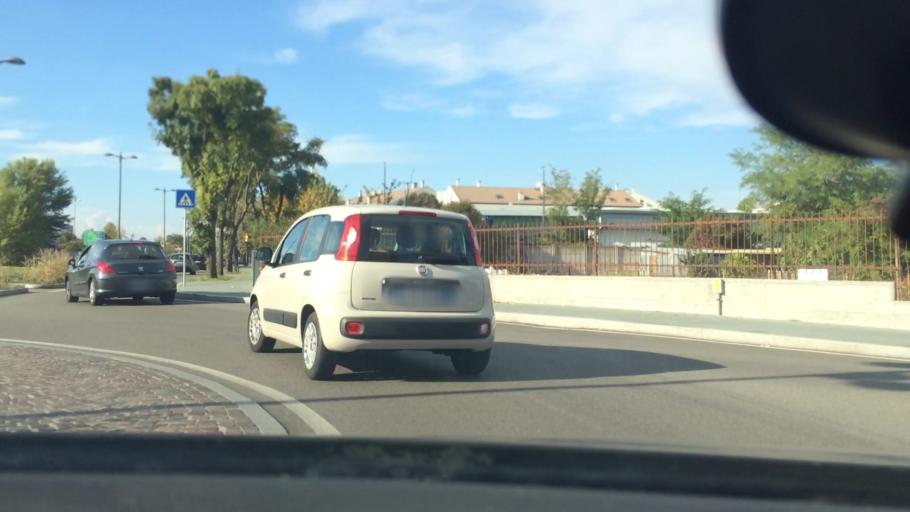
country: IT
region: Lombardy
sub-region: Citta metropolitana di Milano
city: Legnano
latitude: 45.5880
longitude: 8.9020
